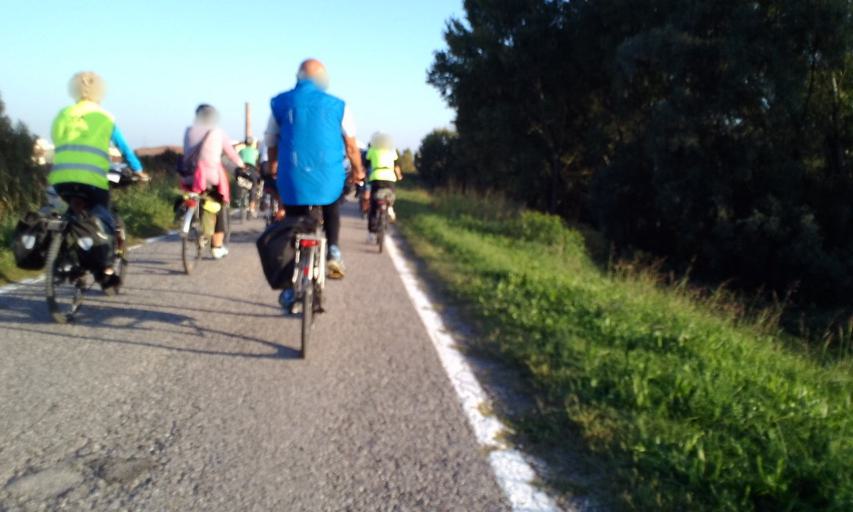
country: IT
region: Lombardy
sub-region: Provincia di Mantova
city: Ostiglia
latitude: 45.0724
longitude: 11.1248
